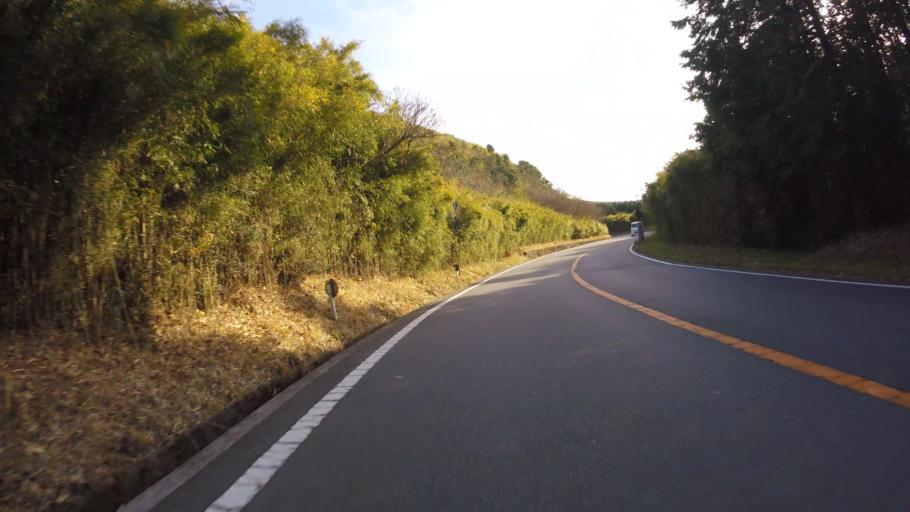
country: JP
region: Kanagawa
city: Yugawara
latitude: 35.1331
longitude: 139.0393
